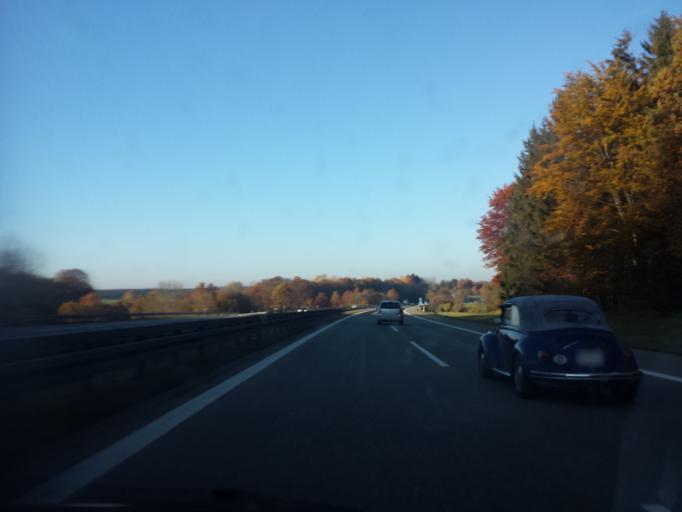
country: DE
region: Bavaria
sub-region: Upper Bavaria
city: Schaftlarn
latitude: 48.0126
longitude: 11.4176
